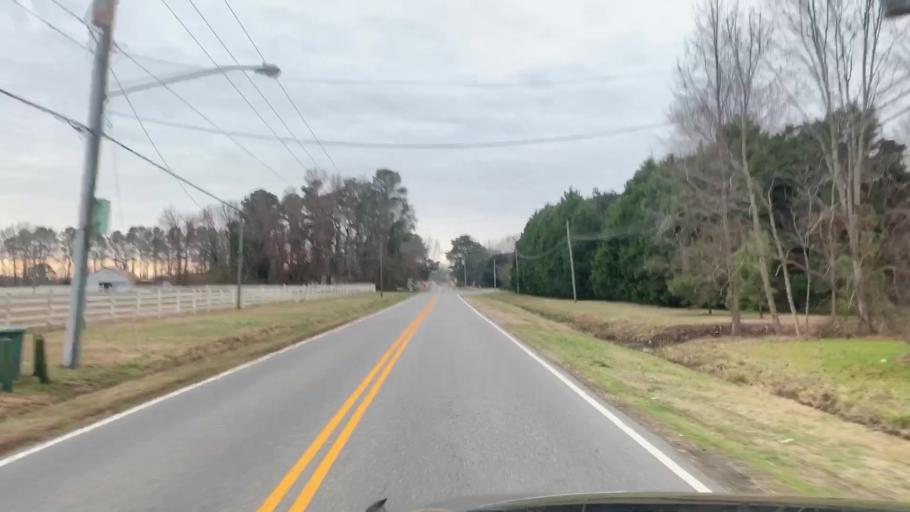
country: US
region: North Carolina
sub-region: Currituck County
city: Moyock
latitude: 36.6397
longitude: -76.2048
